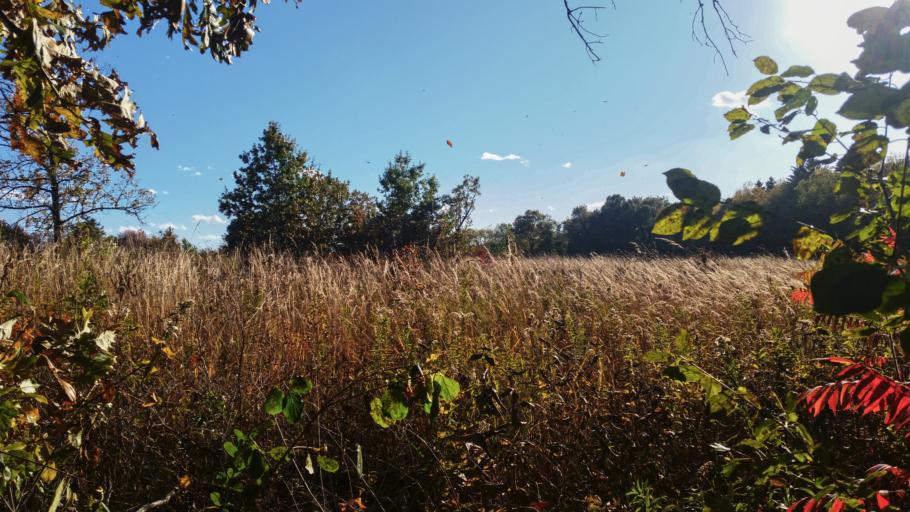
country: US
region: Wisconsin
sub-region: Dane County
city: Shorewood Hills
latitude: 43.0446
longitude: -89.4308
